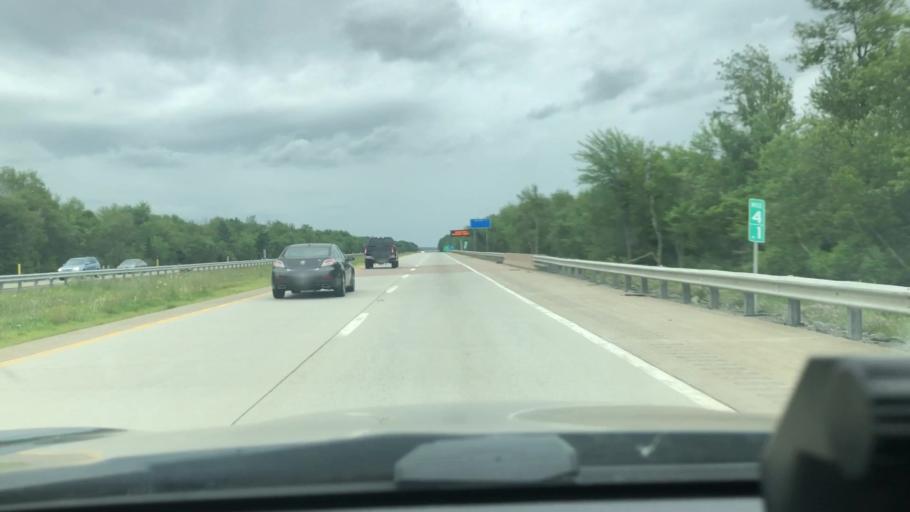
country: US
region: Pennsylvania
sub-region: Monroe County
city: Mount Pocono
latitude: 41.1289
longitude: -75.4006
